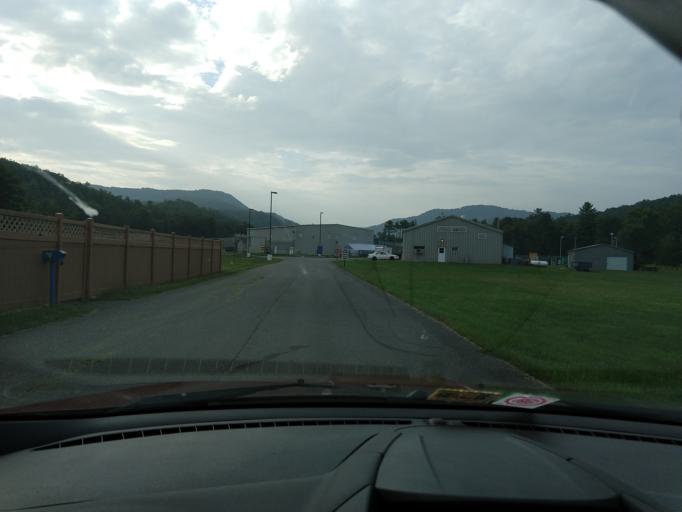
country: US
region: Virginia
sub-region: City of Covington
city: Covington
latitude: 37.9647
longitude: -80.1290
